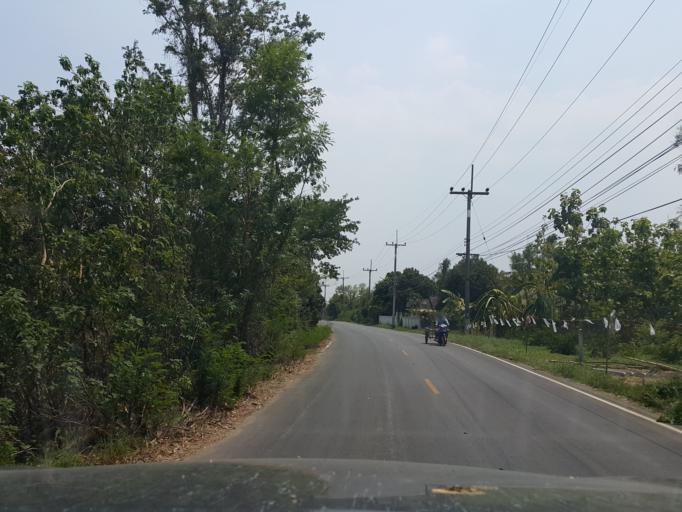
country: TH
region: Lampang
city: Mae Phrik
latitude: 17.5092
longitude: 99.1337
